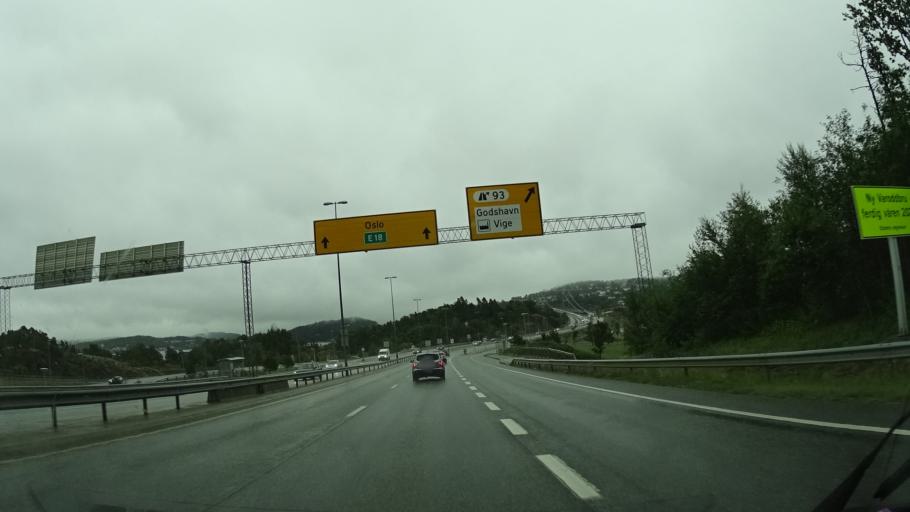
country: NO
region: Vest-Agder
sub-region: Kristiansand
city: Justvik
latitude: 58.1651
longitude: 8.0394
